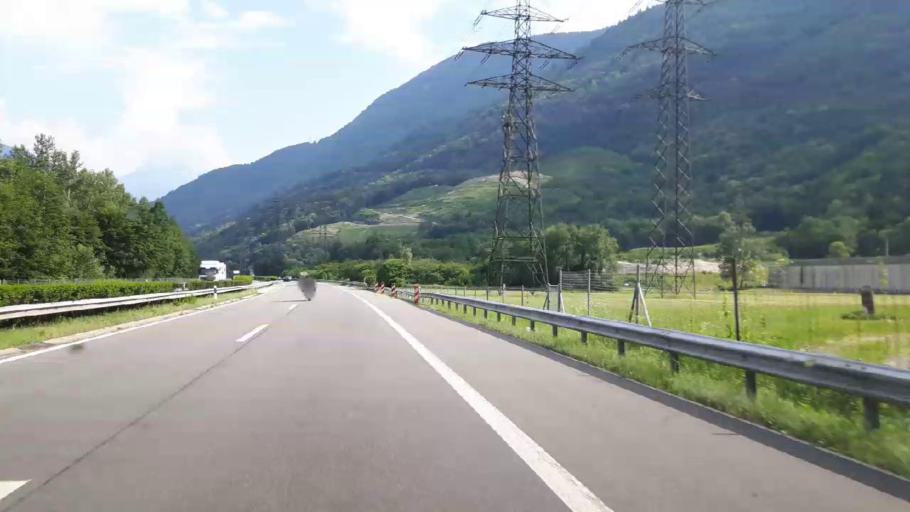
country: CH
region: Ticino
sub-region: Riviera District
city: Claro
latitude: 46.2546
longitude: 9.0094
